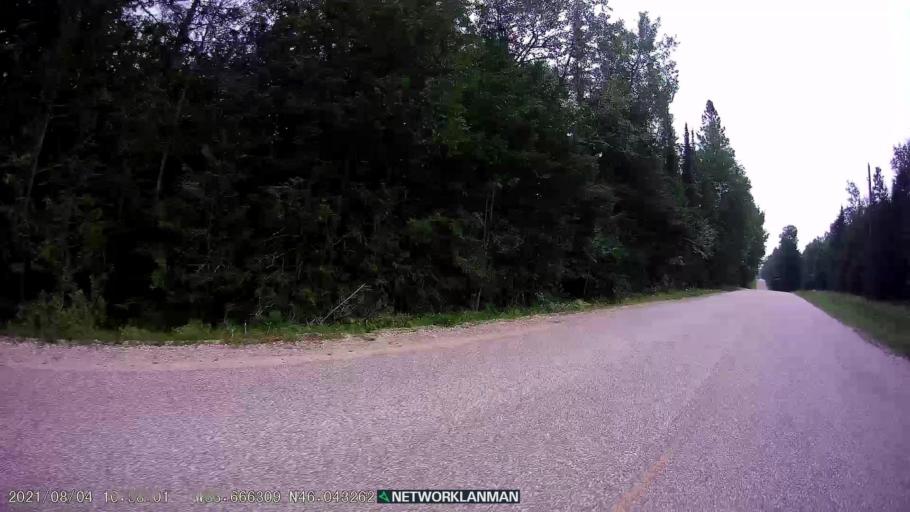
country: CA
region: Ontario
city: Thessalon
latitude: 46.0429
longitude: -83.6664
